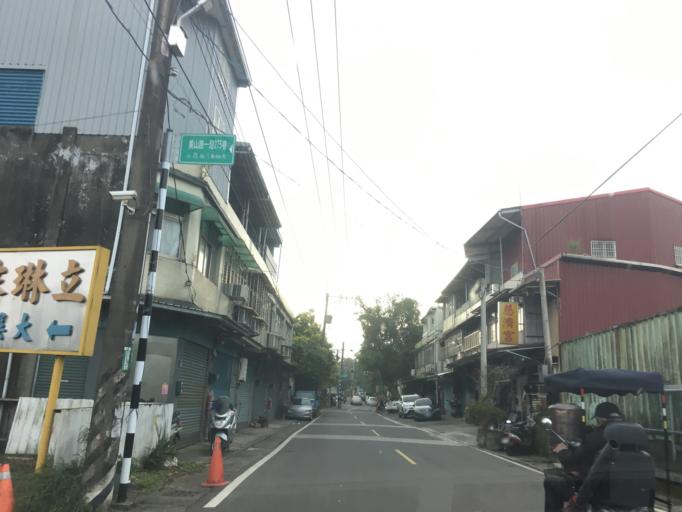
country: TW
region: Taiwan
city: Daxi
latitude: 24.8824
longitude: 121.3029
